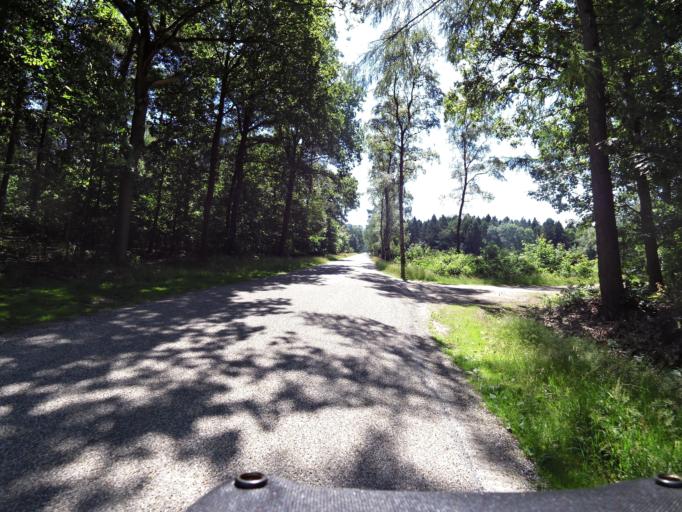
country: NL
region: Overijssel
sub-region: Gemeente Twenterand
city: Den Ham
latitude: 52.5386
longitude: 6.4891
